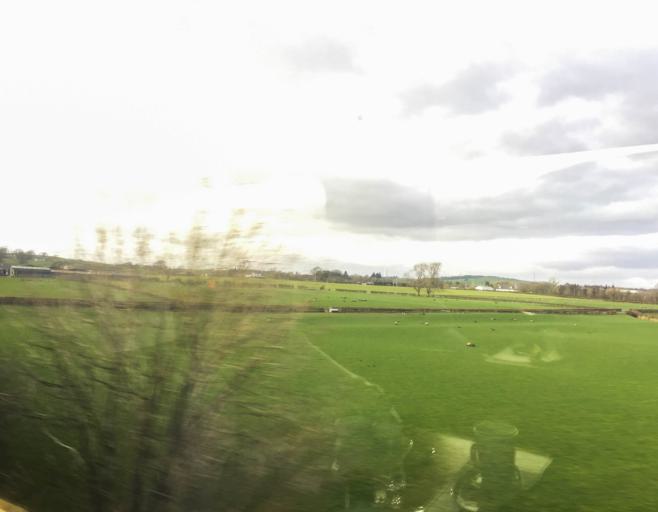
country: GB
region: Scotland
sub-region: Dumfries and Galloway
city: Annan
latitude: 55.0639
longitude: -3.2278
